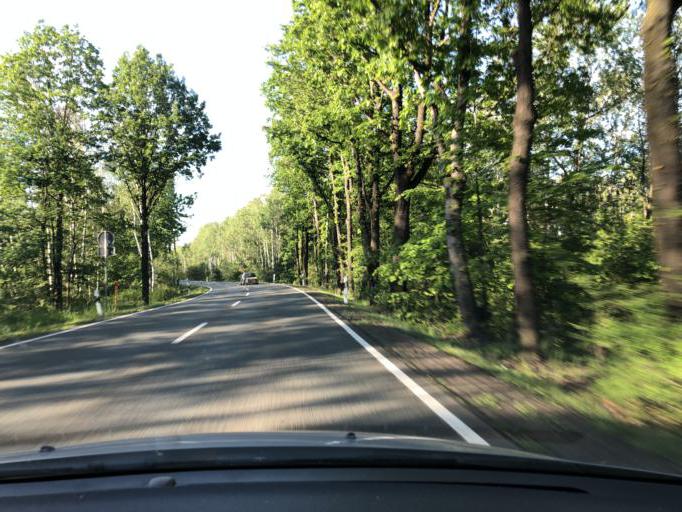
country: DE
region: Thuringia
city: Lucka
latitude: 51.0717
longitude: 12.3199
